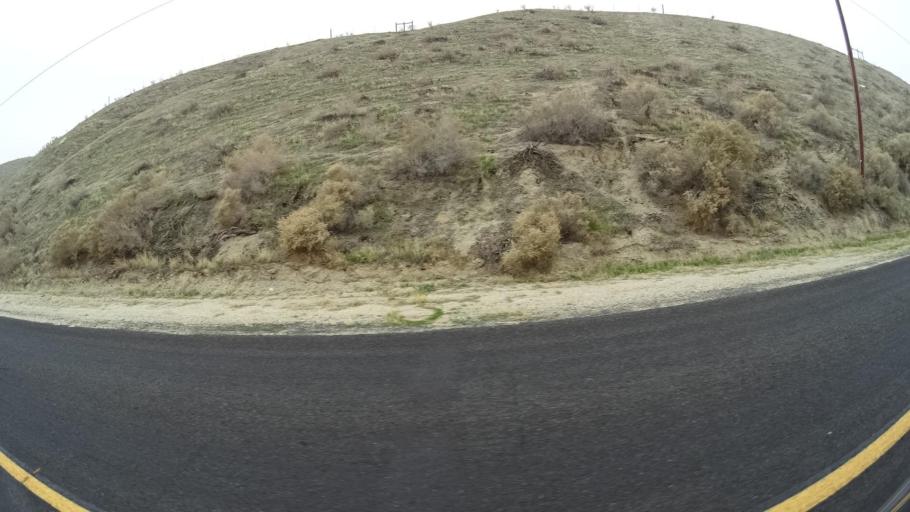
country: US
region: California
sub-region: Kern County
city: Ford City
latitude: 35.2603
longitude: -119.3108
